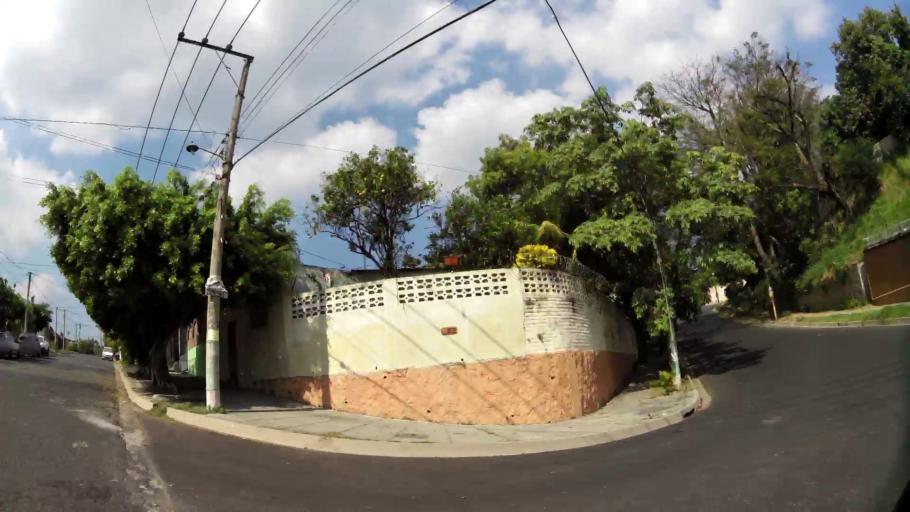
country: SV
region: San Salvador
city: Delgado
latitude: 13.7101
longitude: -89.1678
